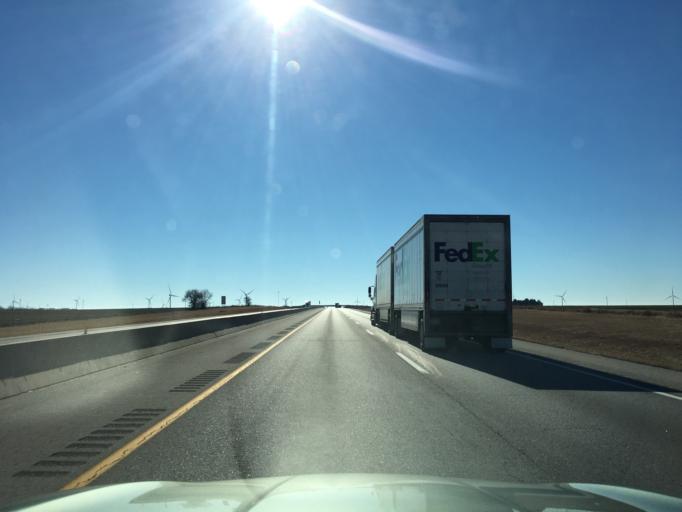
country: US
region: Kansas
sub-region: Sumner County
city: Wellington
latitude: 37.1663
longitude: -97.3395
